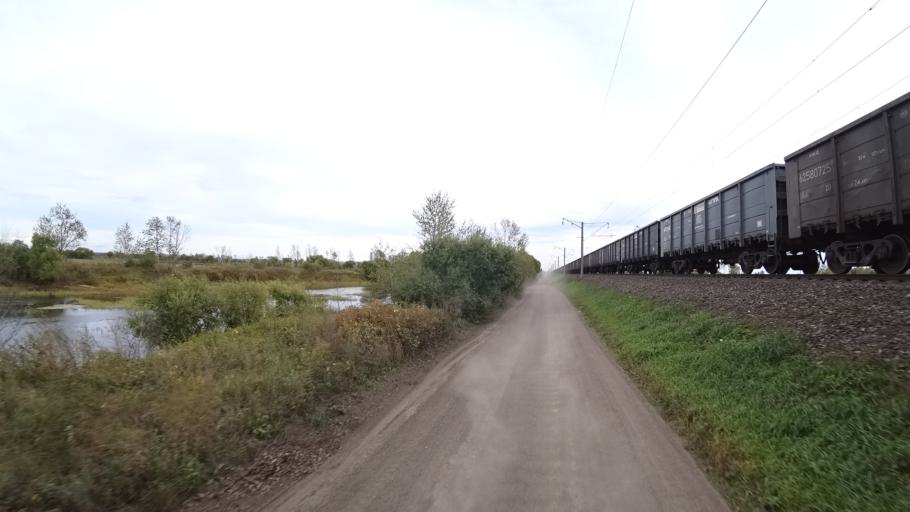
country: RU
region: Amur
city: Arkhara
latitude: 49.3631
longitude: 130.1474
